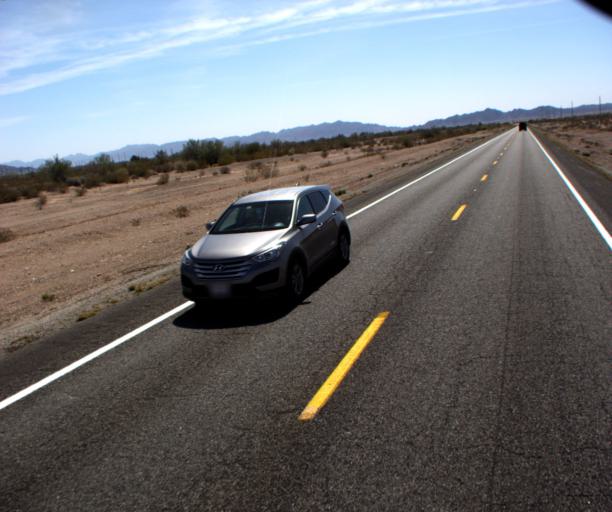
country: US
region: Arizona
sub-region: Yuma County
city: Fortuna Foothills
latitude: 32.8767
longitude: -114.3495
